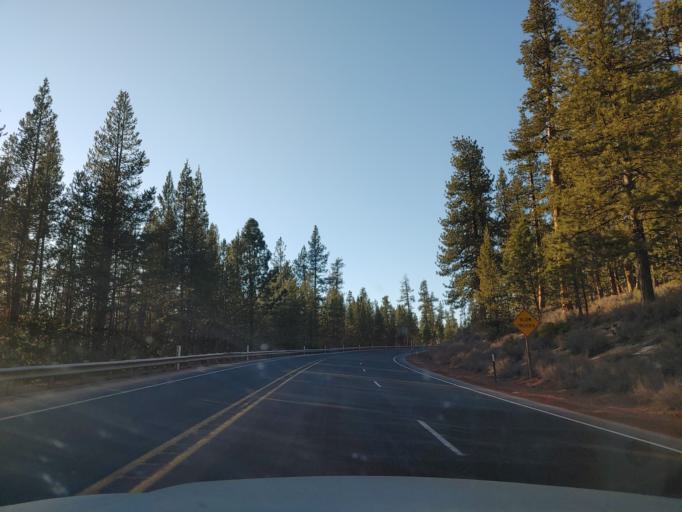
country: US
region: Oregon
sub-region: Deschutes County
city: La Pine
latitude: 43.4433
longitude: -121.8687
